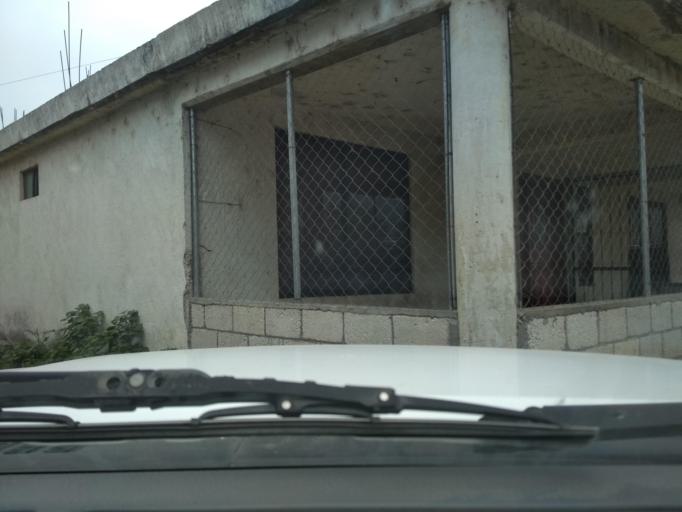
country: MX
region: Veracruz
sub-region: La Perla
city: Chilapa
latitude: 18.9881
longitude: -97.1504
